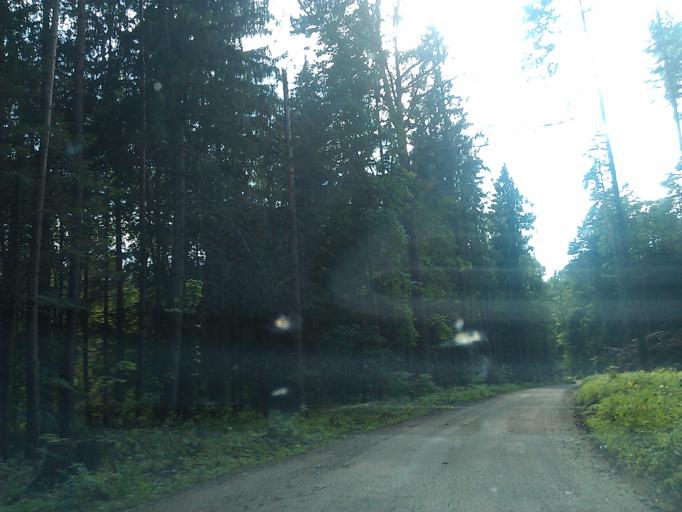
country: LV
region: Saulkrastu
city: Saulkrasti
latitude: 57.3689
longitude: 24.4358
